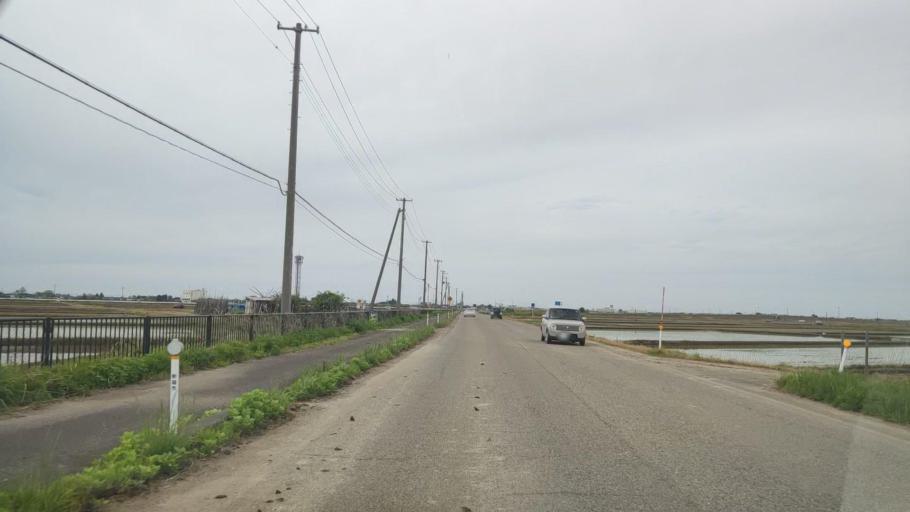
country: JP
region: Niigata
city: Shirone
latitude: 37.7342
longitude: 139.0815
